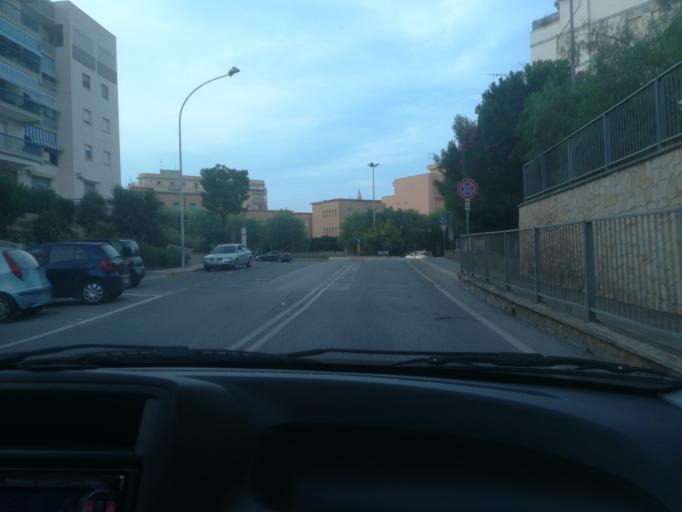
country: IT
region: Apulia
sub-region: Provincia di Bari
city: Monopoli
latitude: 40.9471
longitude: 17.3026
